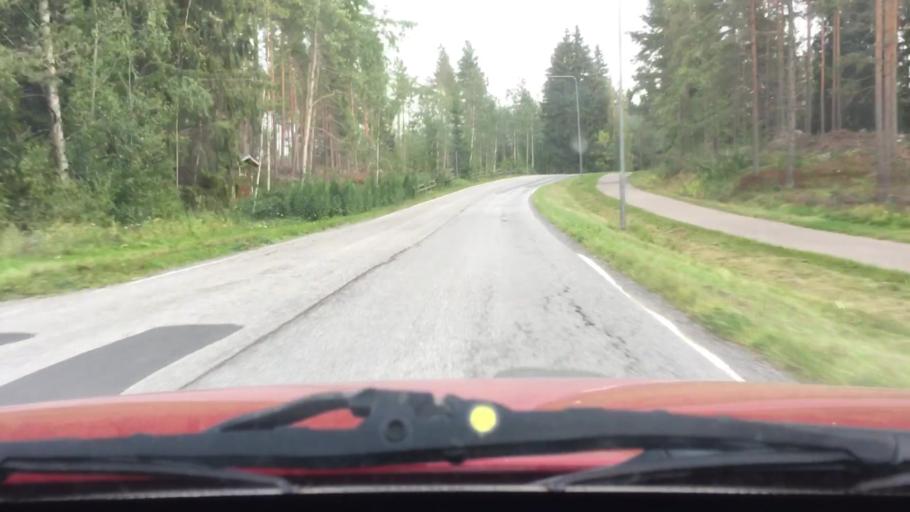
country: FI
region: Varsinais-Suomi
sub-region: Turku
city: Masku
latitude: 60.5550
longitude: 22.1300
